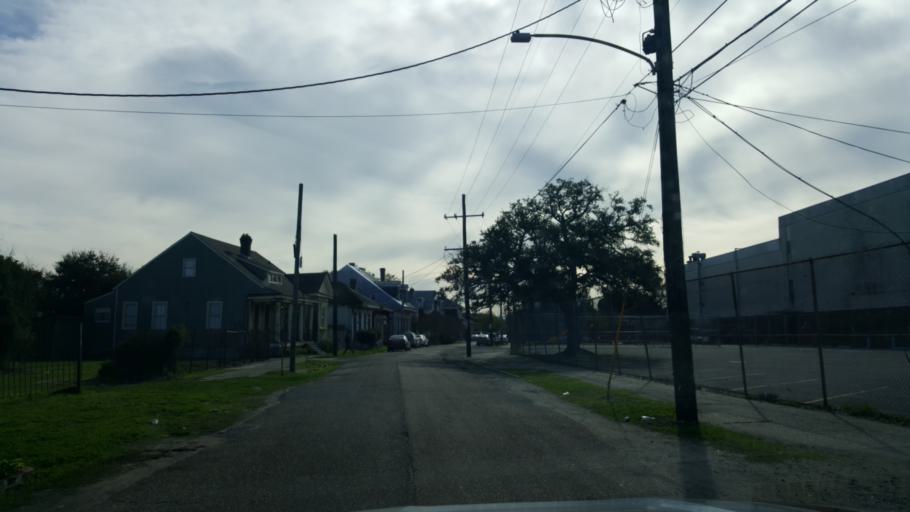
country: US
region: Louisiana
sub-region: Orleans Parish
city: New Orleans
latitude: 29.9697
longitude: -90.0652
